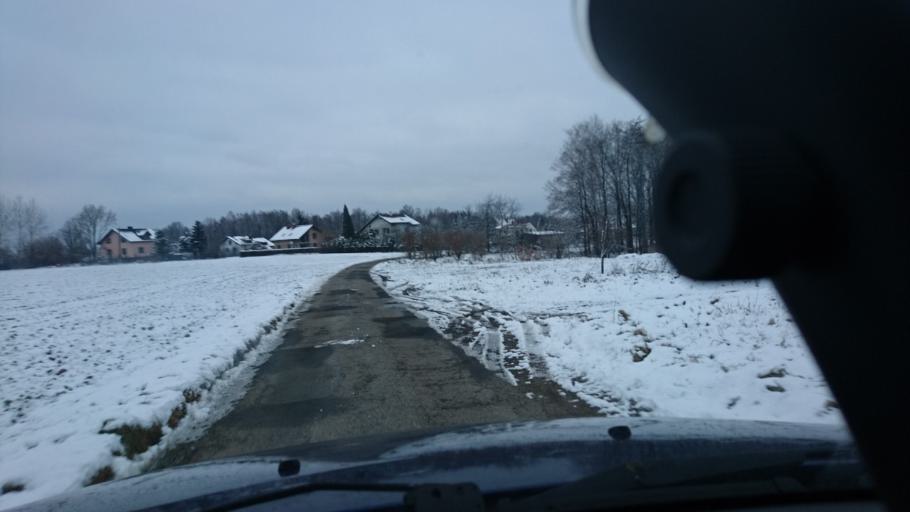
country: PL
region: Silesian Voivodeship
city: Janowice
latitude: 49.8634
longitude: 19.1103
